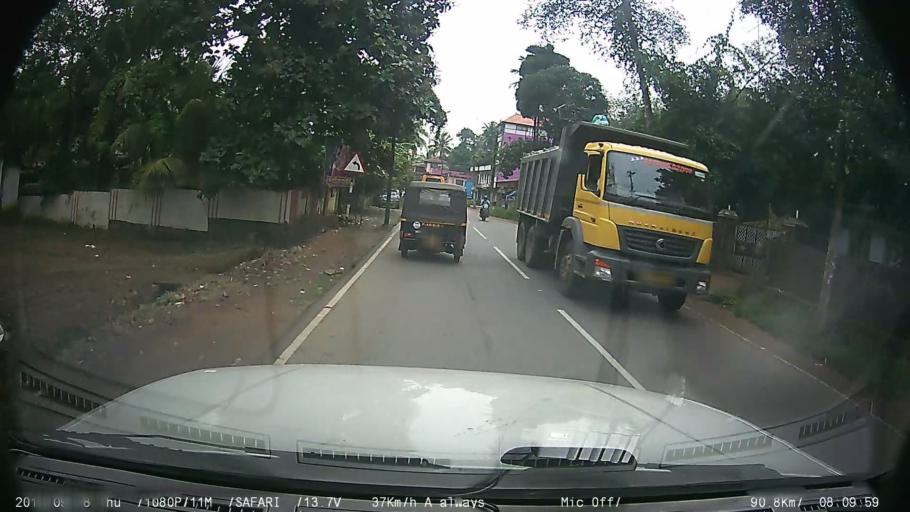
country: IN
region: Kerala
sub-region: Kottayam
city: Kottayam
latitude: 9.6018
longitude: 76.5889
